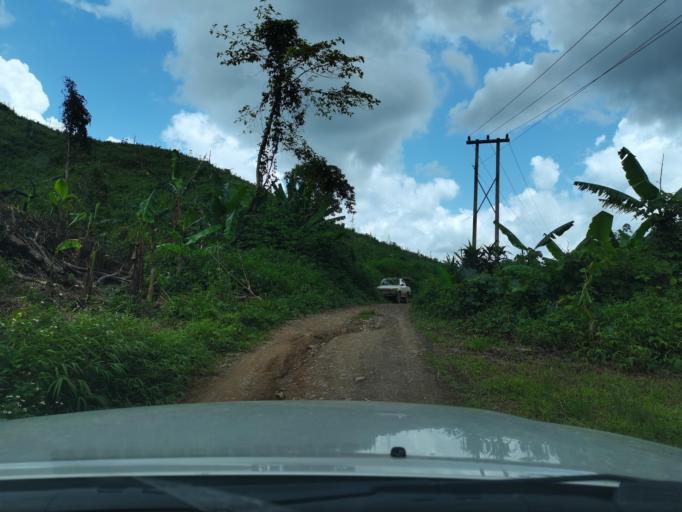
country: LA
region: Loungnamtha
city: Muang Long
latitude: 20.7640
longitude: 101.0176
